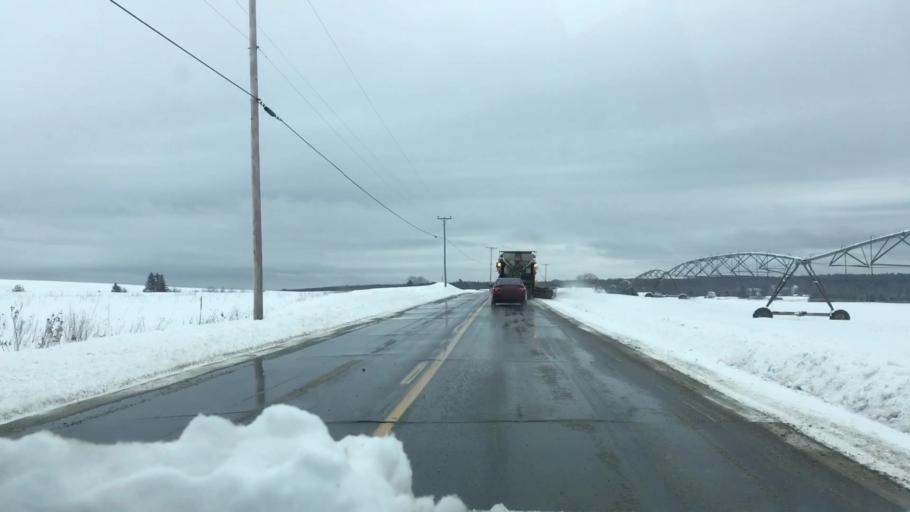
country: US
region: Maine
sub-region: Penobscot County
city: Garland
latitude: 44.9784
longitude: -69.1030
